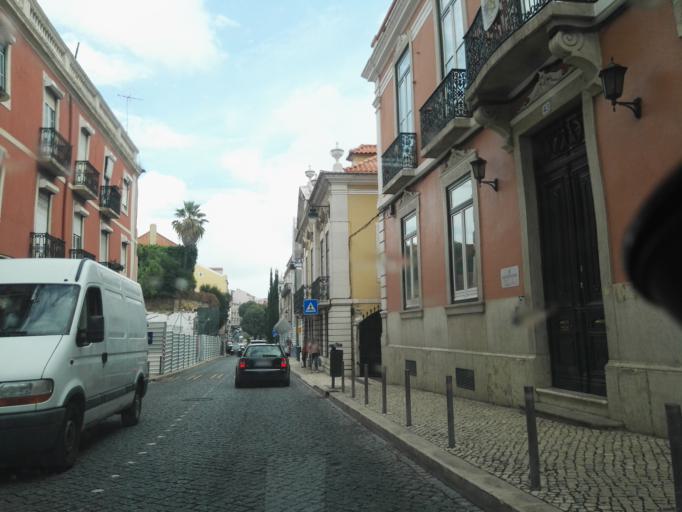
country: PT
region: Setubal
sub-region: Almada
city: Cacilhas
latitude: 38.7056
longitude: -9.1601
